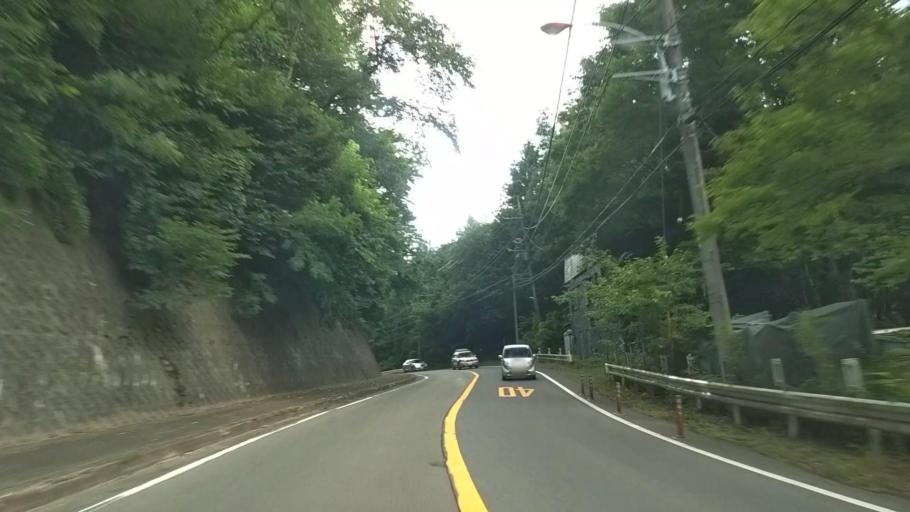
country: JP
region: Tokyo
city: Hachioji
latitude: 35.5619
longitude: 139.2364
